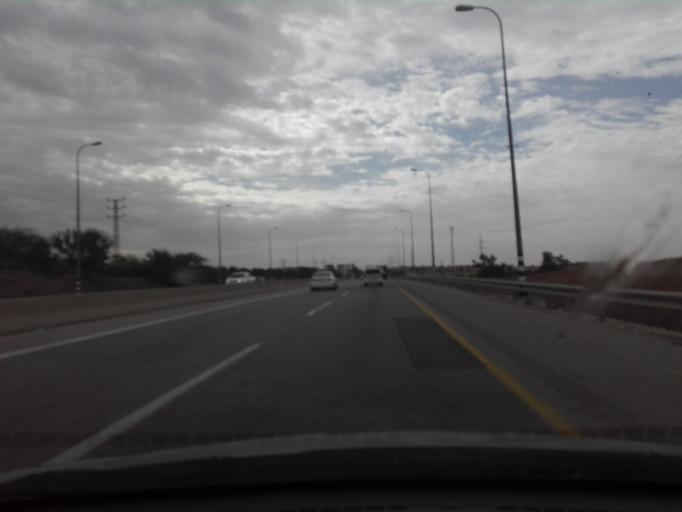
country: IL
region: Southern District
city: Lehavim
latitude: 31.3562
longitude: 34.7941
